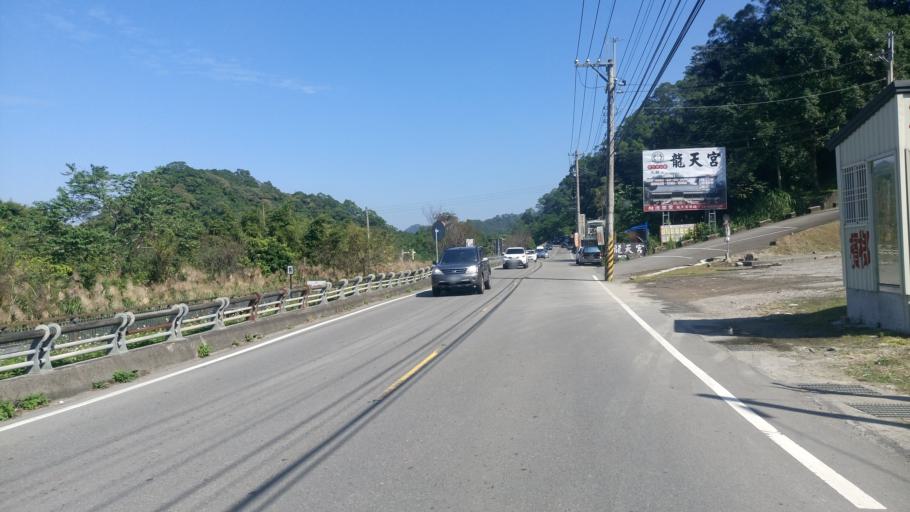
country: TW
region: Taiwan
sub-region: Hsinchu
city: Zhubei
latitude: 24.7173
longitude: 121.1561
